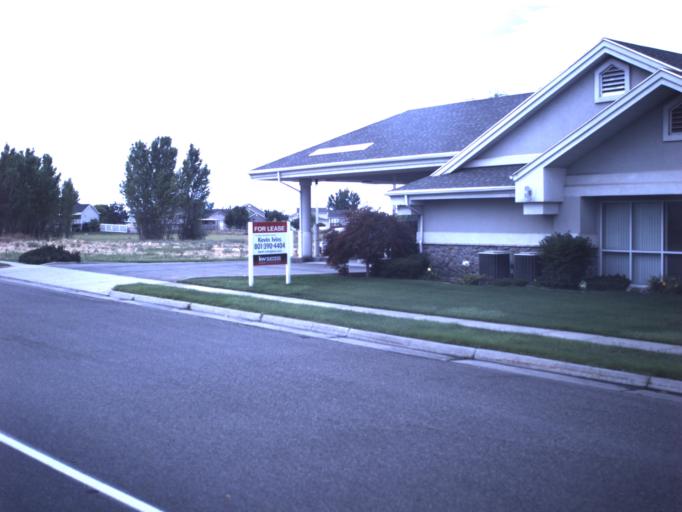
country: US
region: Utah
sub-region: Weber County
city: West Haven
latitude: 41.1759
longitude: -112.0645
